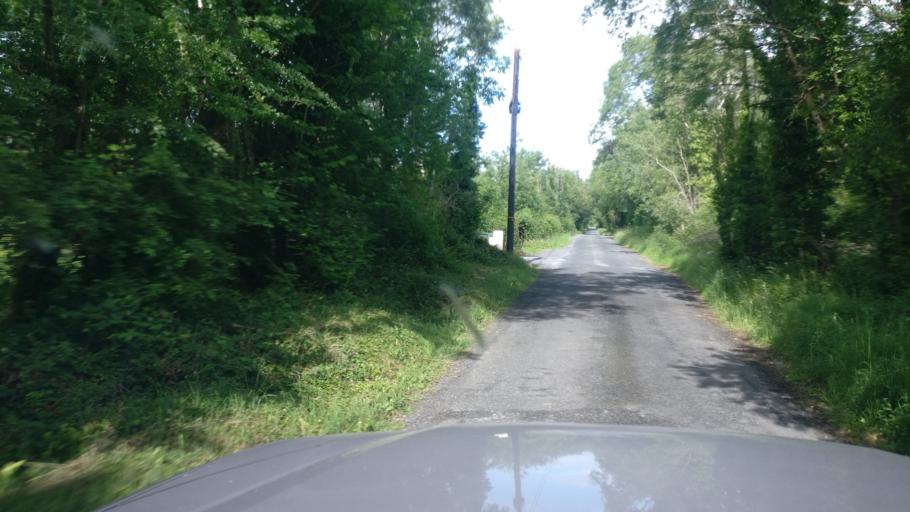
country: IE
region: Connaught
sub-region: County Galway
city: Gort
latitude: 53.0767
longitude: -8.7639
